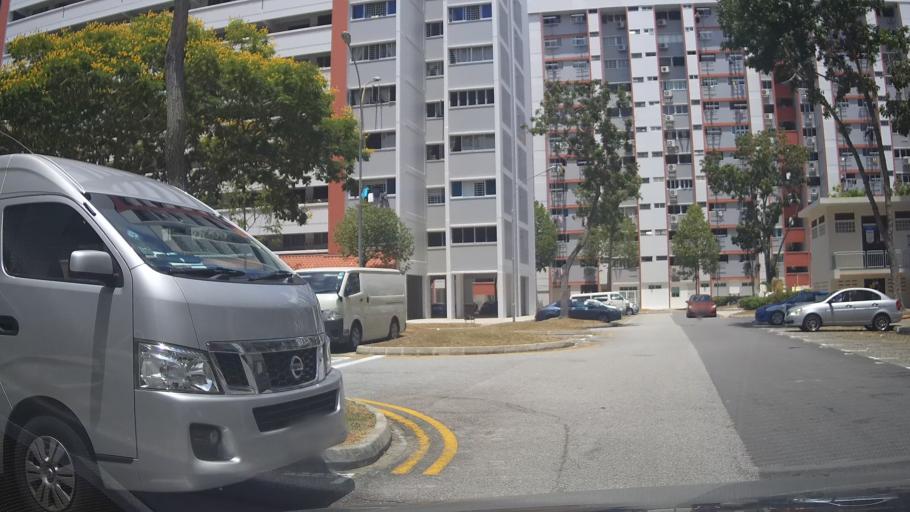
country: SG
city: Singapore
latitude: 1.3574
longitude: 103.9513
